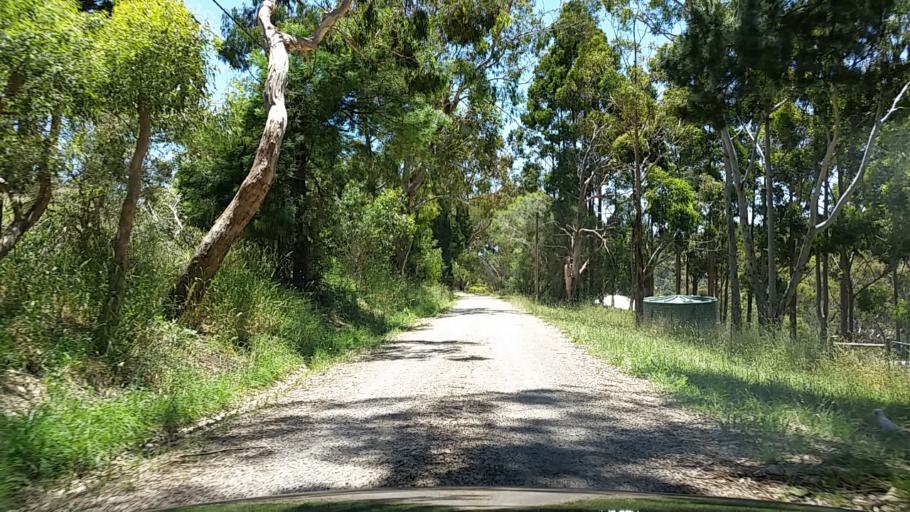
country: AU
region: South Australia
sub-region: Adelaide Hills
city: Crafers
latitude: -34.9961
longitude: 138.6805
